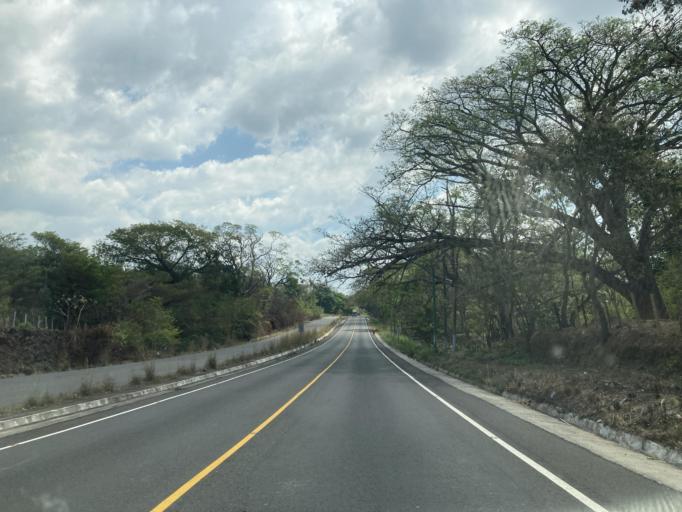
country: GT
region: Santa Rosa
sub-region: Municipio de Taxisco
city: Taxisco
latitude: 14.0911
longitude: -90.5142
